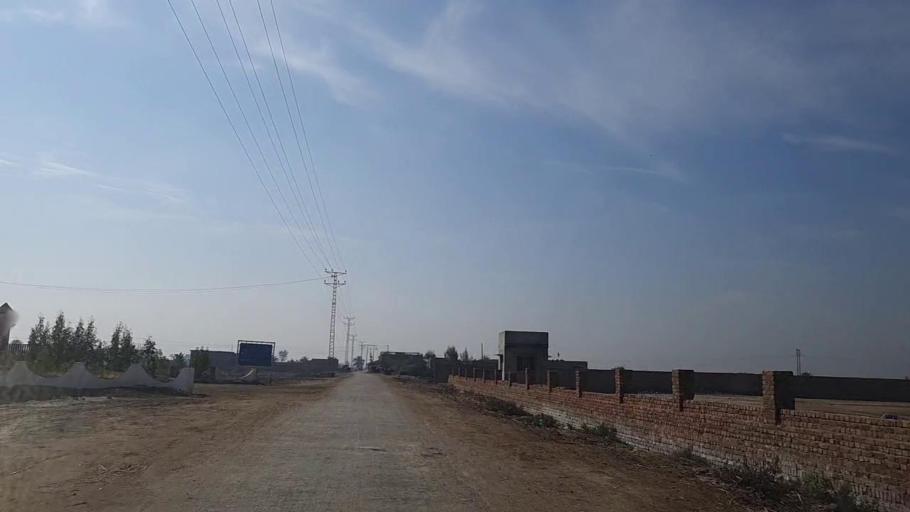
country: PK
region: Sindh
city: Mirpur Khas
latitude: 25.5042
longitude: 69.0001
